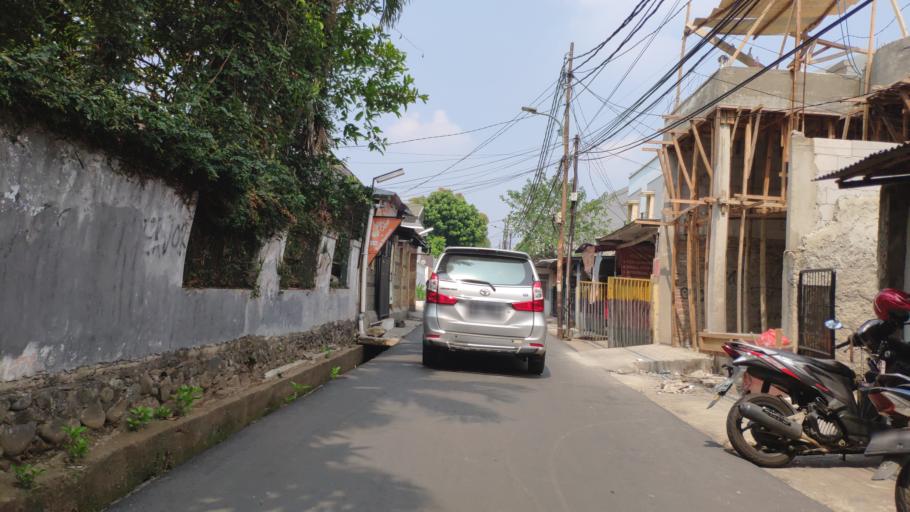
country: ID
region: Banten
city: South Tangerang
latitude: -6.2713
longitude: 106.7751
